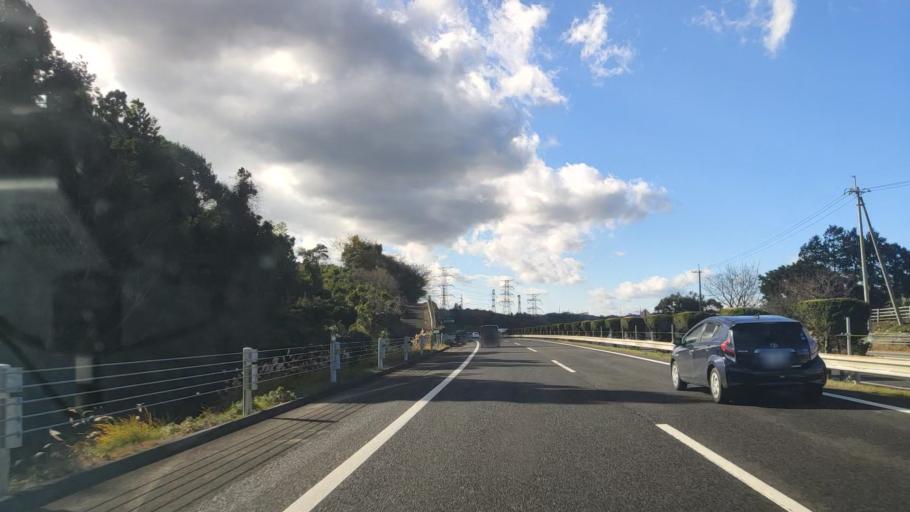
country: JP
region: Ehime
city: Niihama
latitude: 33.9452
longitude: 133.4092
